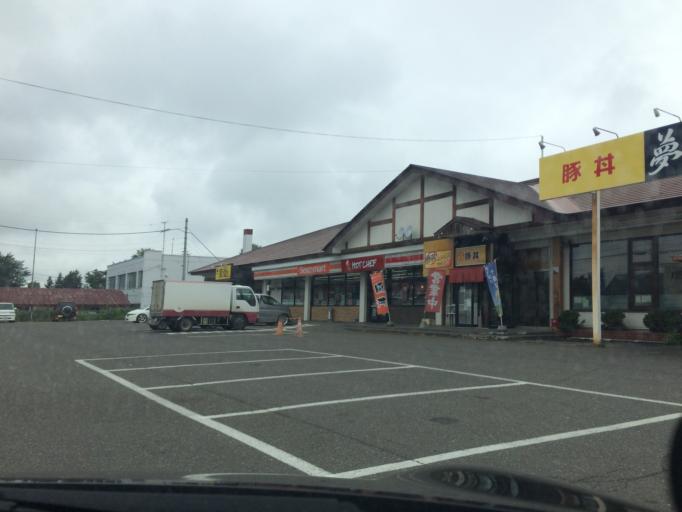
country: JP
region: Hokkaido
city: Obihiro
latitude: 42.9269
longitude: 143.1292
